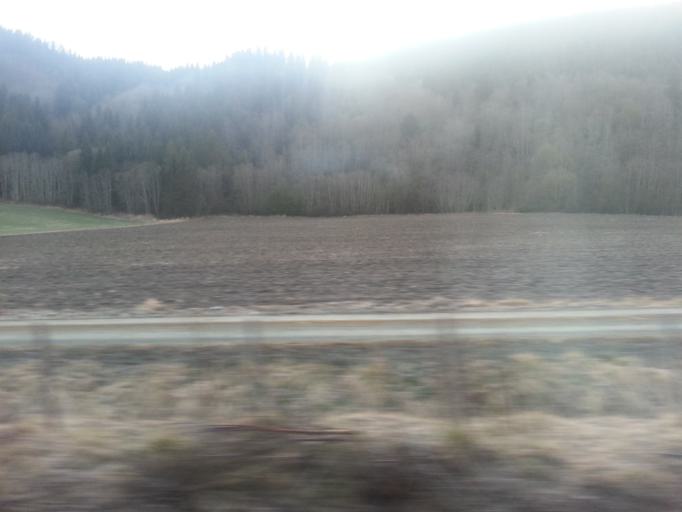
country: NO
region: Sor-Trondelag
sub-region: Melhus
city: Melhus
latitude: 63.2438
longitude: 10.2798
